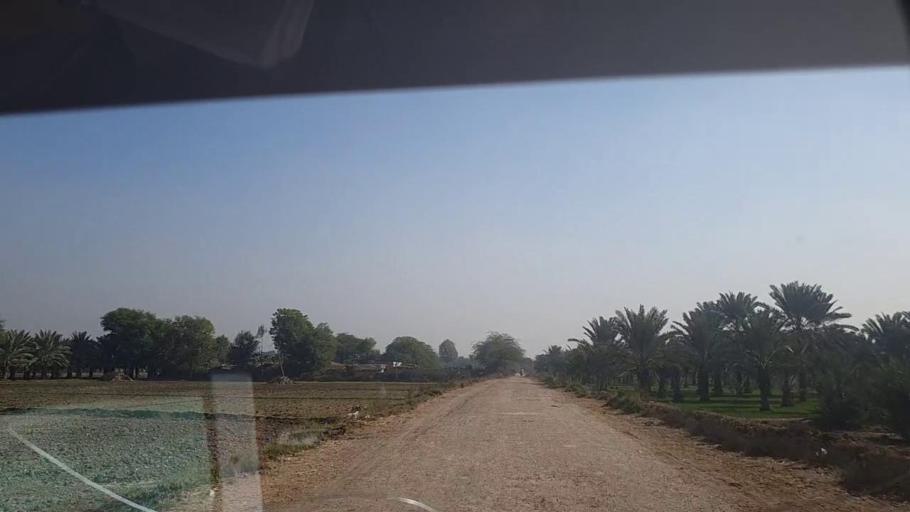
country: PK
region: Sindh
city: Kot Diji
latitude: 27.4351
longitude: 68.6807
